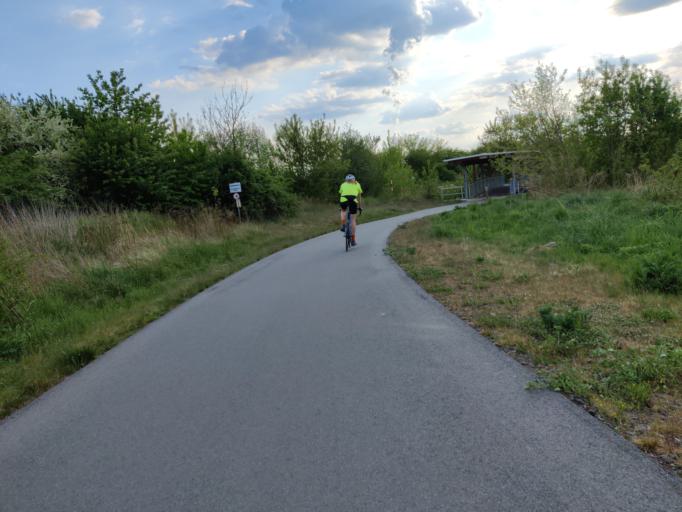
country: DE
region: Saxony
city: Espenhain
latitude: 51.2216
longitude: 12.4579
